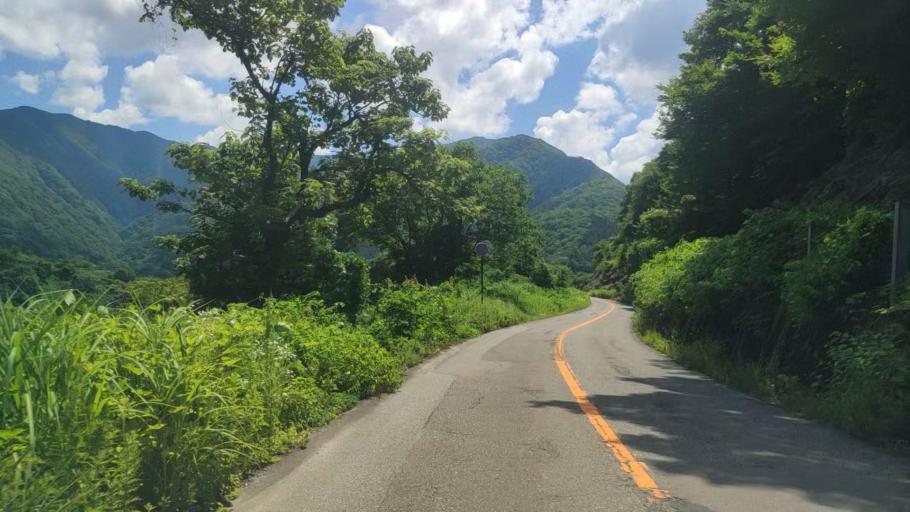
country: JP
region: Fukui
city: Ono
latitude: 35.9146
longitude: 136.5288
